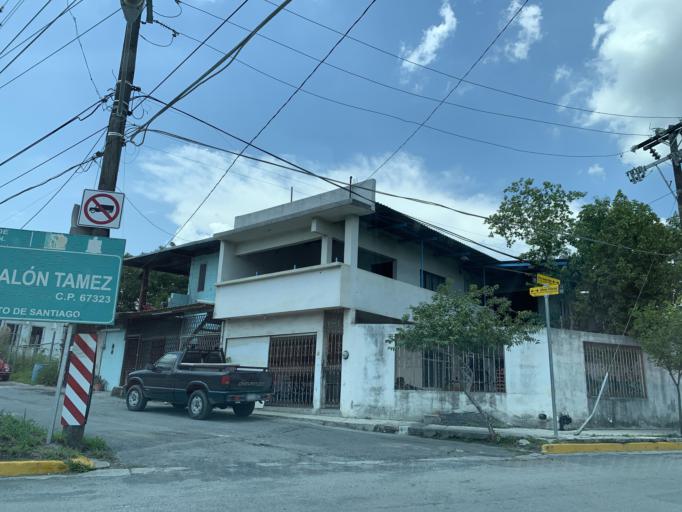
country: MX
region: Nuevo Leon
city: Santiago
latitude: 25.3980
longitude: -100.1274
